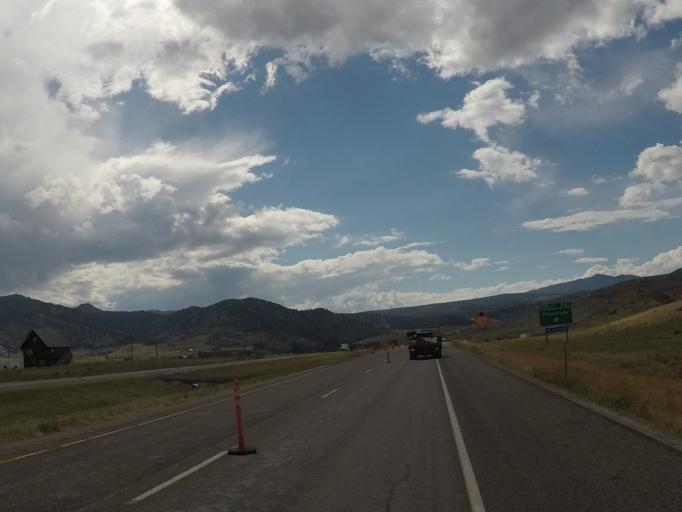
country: US
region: Montana
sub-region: Jefferson County
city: Whitehall
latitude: 45.9047
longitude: -112.2374
